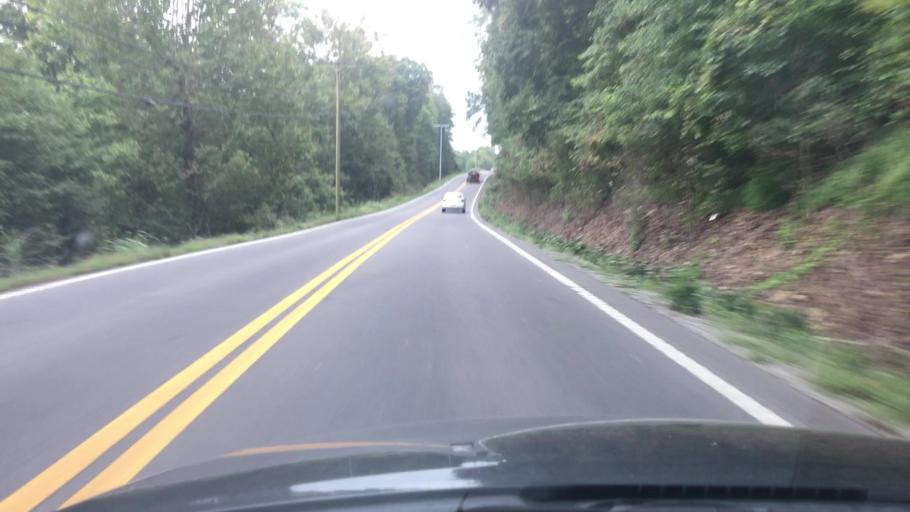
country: US
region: Tennessee
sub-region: Cheatham County
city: Ashland City
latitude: 36.2781
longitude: -87.0962
